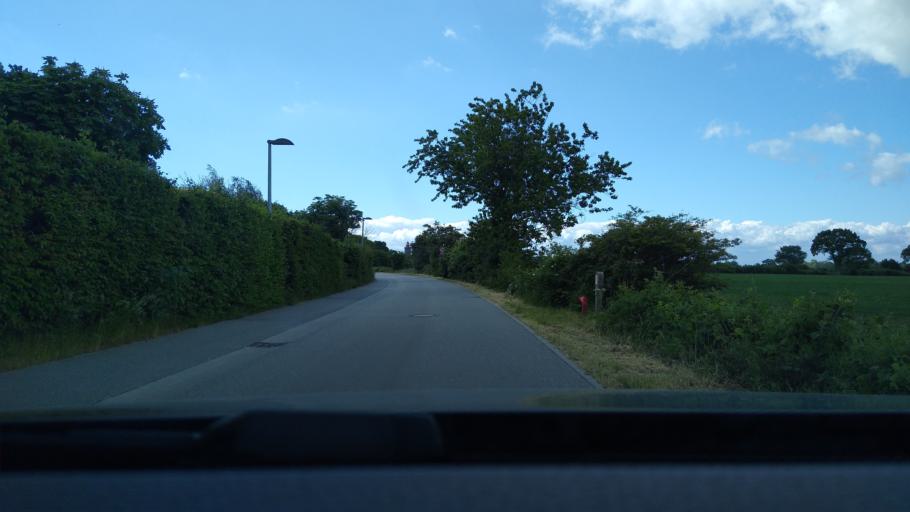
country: DE
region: Schleswig-Holstein
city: Dahme
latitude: 54.2083
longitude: 11.0895
